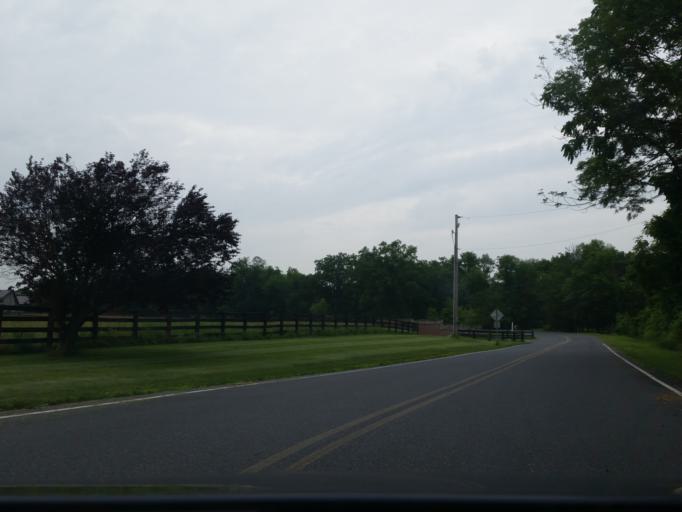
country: US
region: Pennsylvania
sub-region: Dauphin County
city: Skyline View
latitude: 40.4015
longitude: -76.6473
